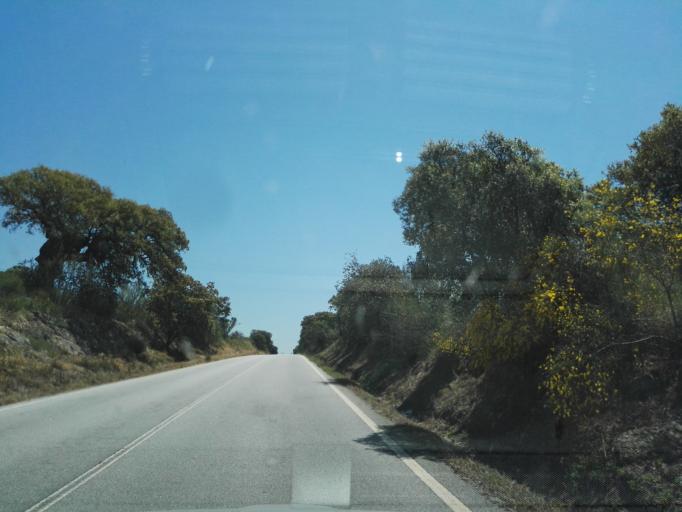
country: PT
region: Portalegre
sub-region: Arronches
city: Arronches
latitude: 39.0058
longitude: -7.2308
